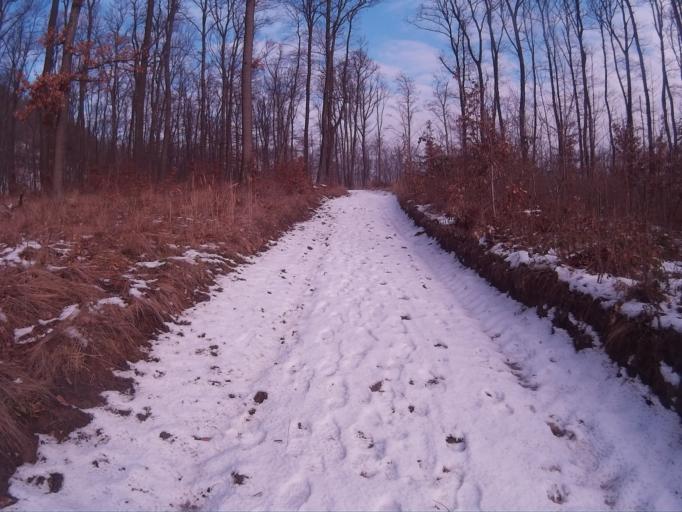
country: HU
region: Komarom-Esztergom
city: Tardos
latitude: 47.6761
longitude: 18.5049
